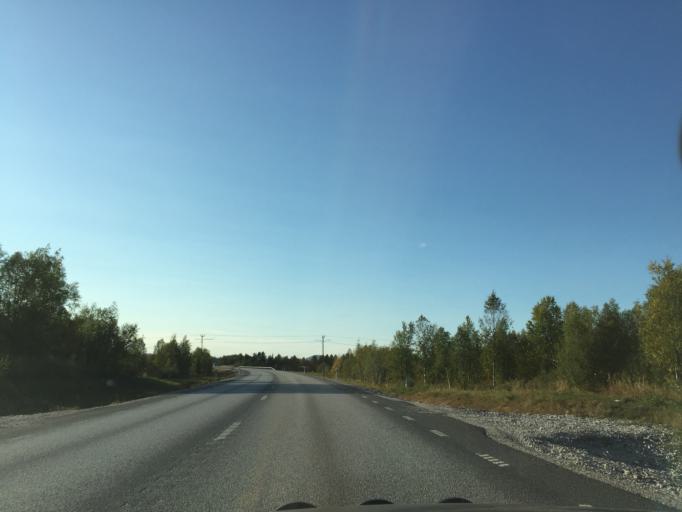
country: SE
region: Norrbotten
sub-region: Gallivare Kommun
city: Malmberget
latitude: 67.6431
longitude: 21.0536
